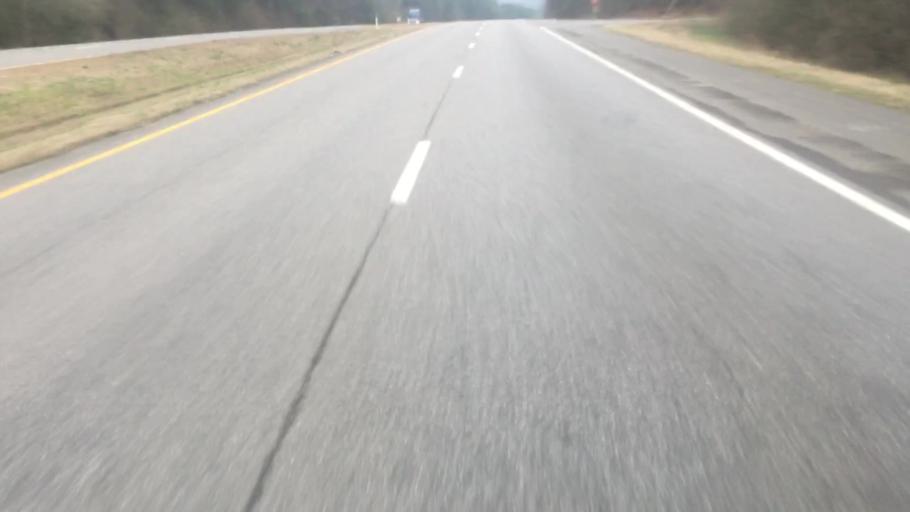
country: US
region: Alabama
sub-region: Jefferson County
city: Graysville
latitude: 33.6776
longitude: -86.9725
